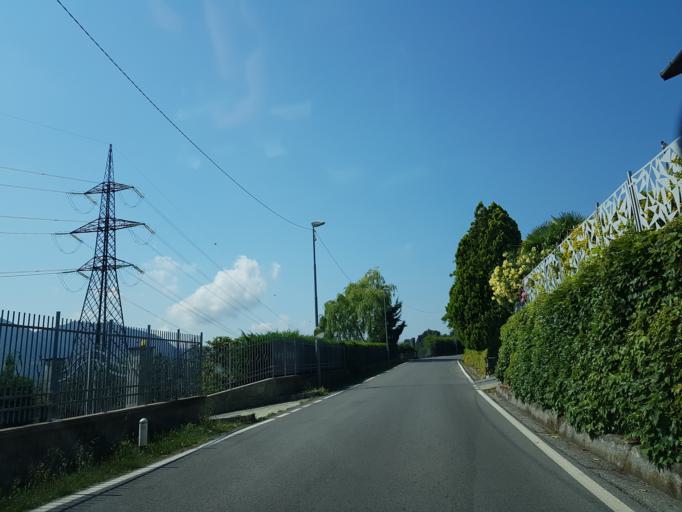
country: IT
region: Liguria
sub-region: Provincia di Genova
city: Pedemonte
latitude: 44.4906
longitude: 8.9129
